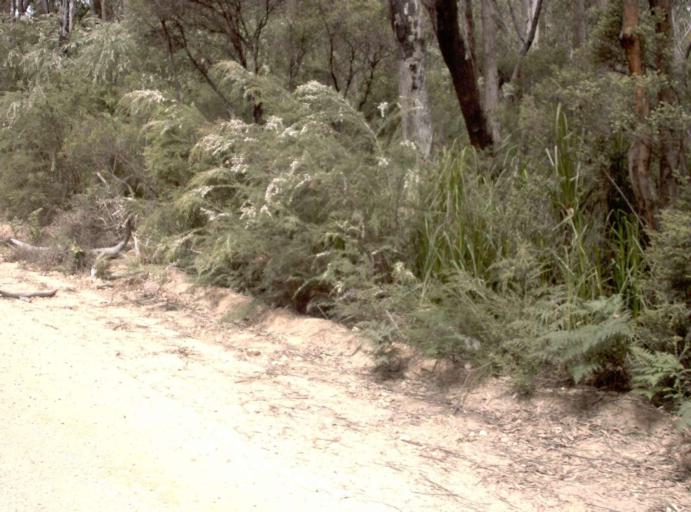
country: AU
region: Victoria
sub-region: East Gippsland
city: Lakes Entrance
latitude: -37.6751
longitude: 148.6295
